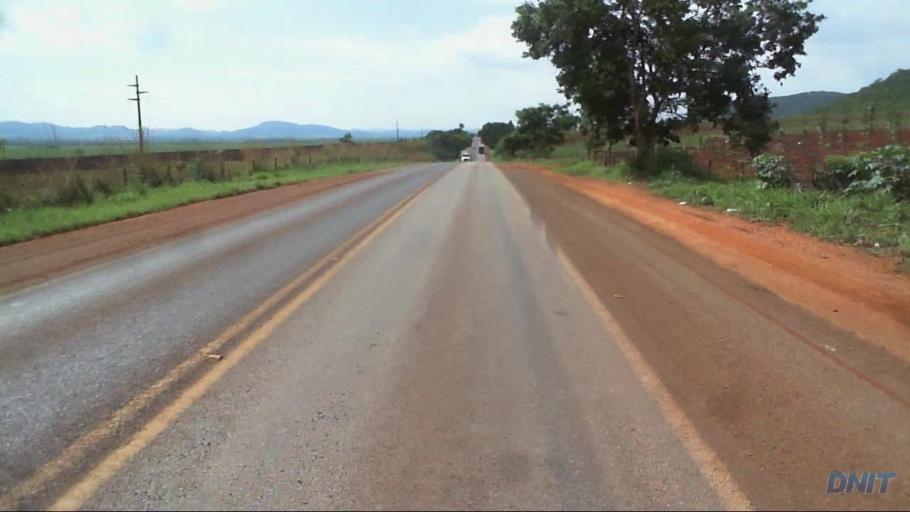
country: BR
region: Goias
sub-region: Barro Alto
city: Barro Alto
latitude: -14.9951
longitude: -48.9069
